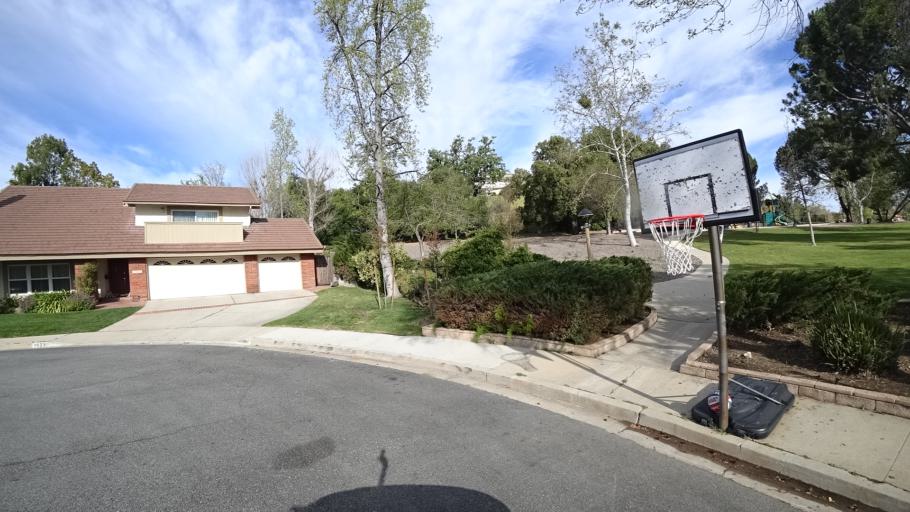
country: US
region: California
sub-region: Ventura County
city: Thousand Oaks
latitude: 34.1518
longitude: -118.8358
